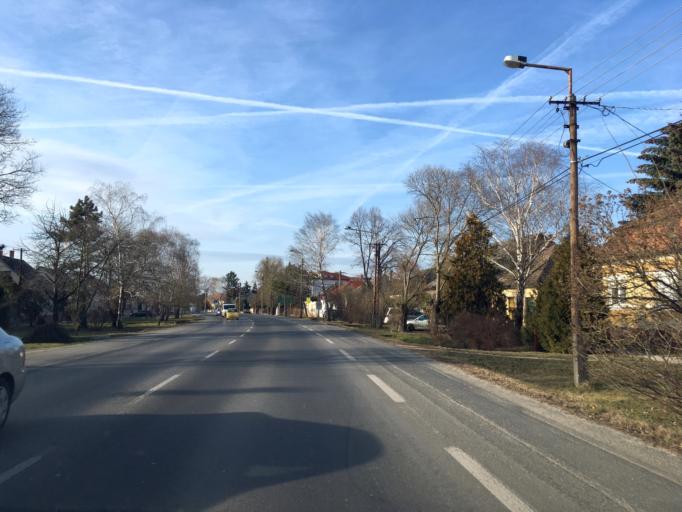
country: HU
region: Gyor-Moson-Sopron
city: Otteveny
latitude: 47.7270
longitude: 17.4891
